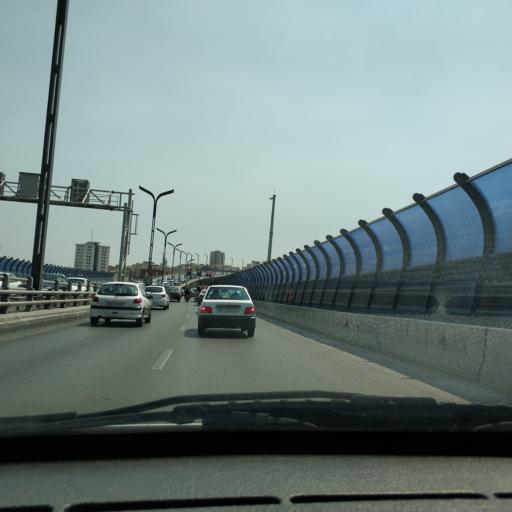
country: IR
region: Tehran
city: Tajrish
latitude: 35.7828
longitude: 51.4345
